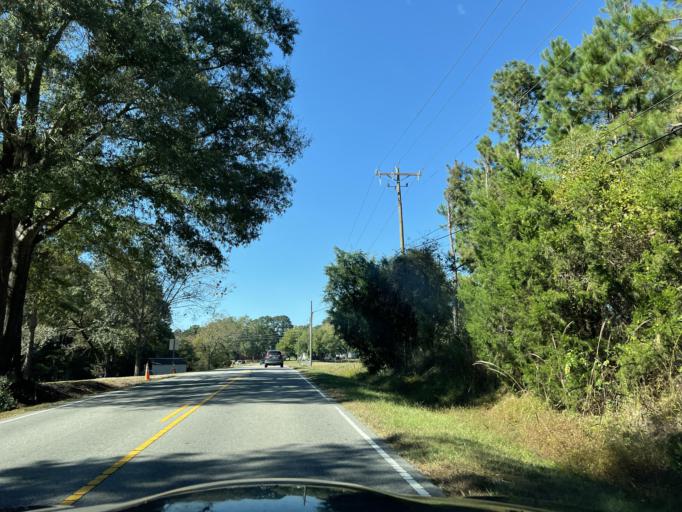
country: US
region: North Carolina
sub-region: Wake County
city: Garner
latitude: 35.6905
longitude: -78.5382
